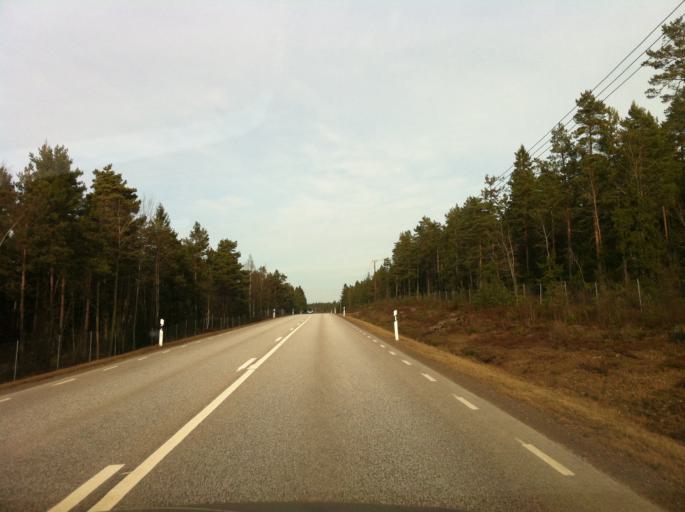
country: SE
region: Vaestra Goetaland
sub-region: Gullspangs Kommun
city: Gullspang
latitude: 58.9404
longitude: 14.0427
